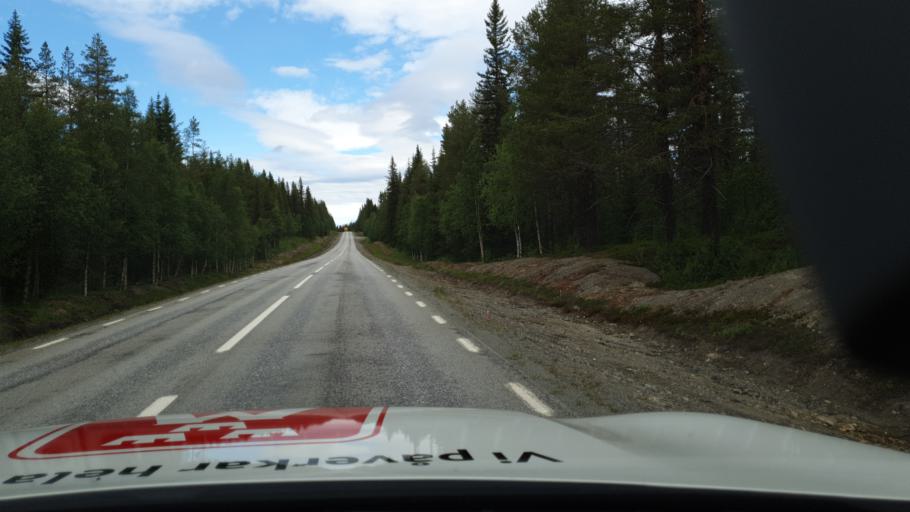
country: SE
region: Vaesterbotten
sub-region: Storumans Kommun
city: Fristad
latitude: 65.3453
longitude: 16.6017
